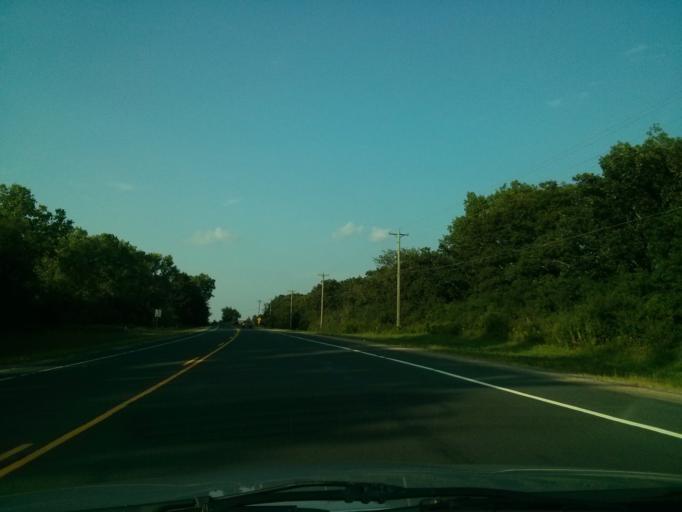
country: US
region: Wisconsin
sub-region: Saint Croix County
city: North Hudson
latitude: 44.9944
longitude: -92.6778
